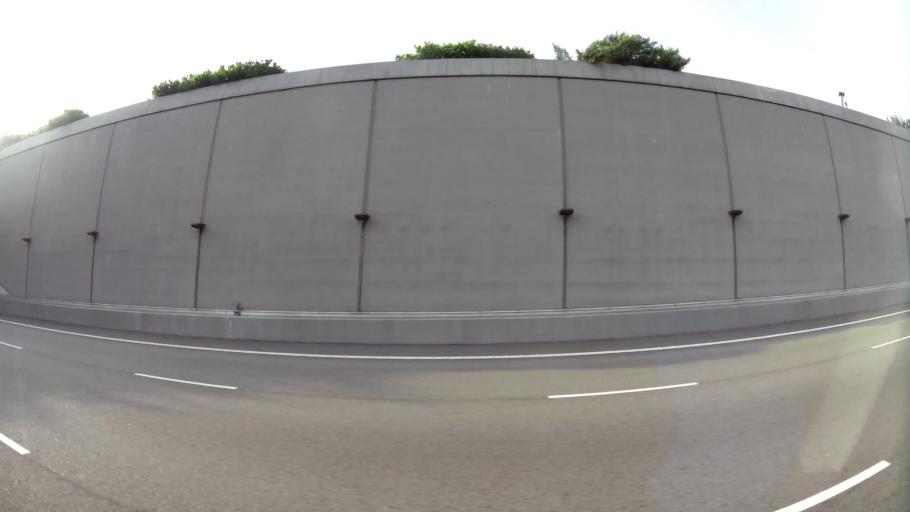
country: SG
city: Singapore
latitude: 1.2701
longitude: 103.8578
